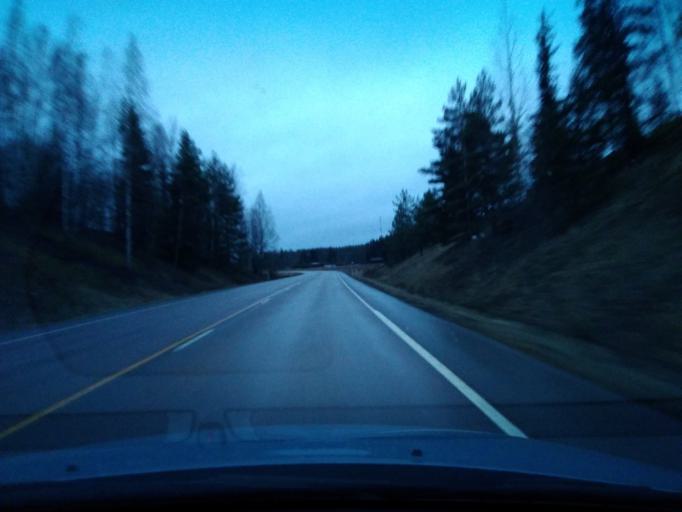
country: FI
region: Uusimaa
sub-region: Porvoo
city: Askola
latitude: 60.4718
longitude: 25.5694
